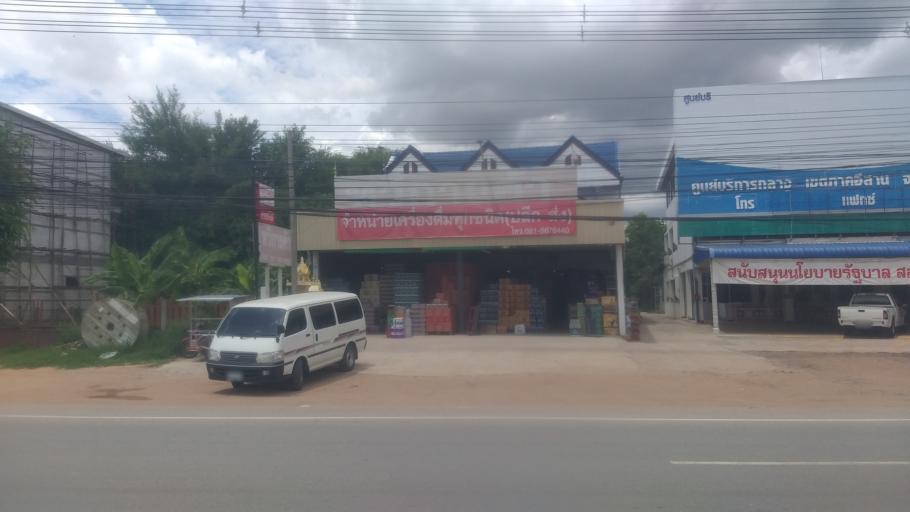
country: TH
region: Nakhon Ratchasima
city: Nakhon Ratchasima
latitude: 15.0730
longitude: 102.1183
